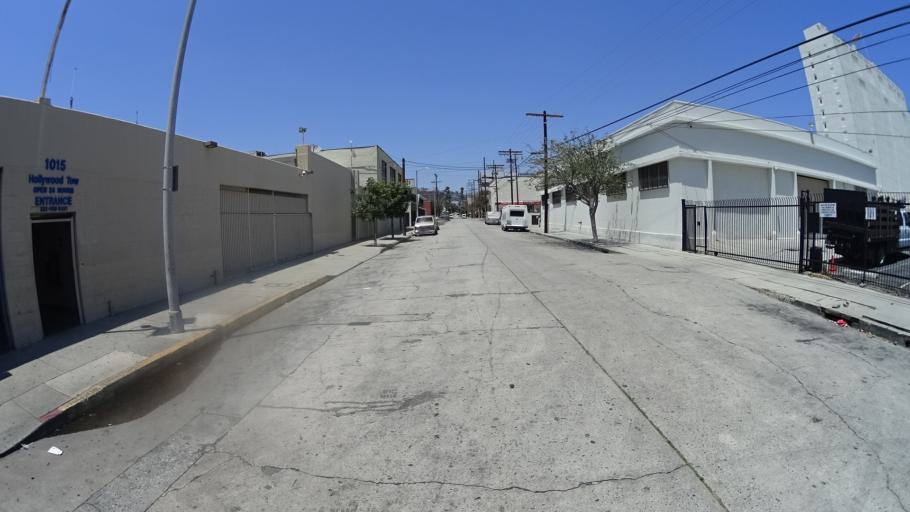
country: US
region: California
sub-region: Los Angeles County
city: Hollywood
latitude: 34.0892
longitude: -118.3405
